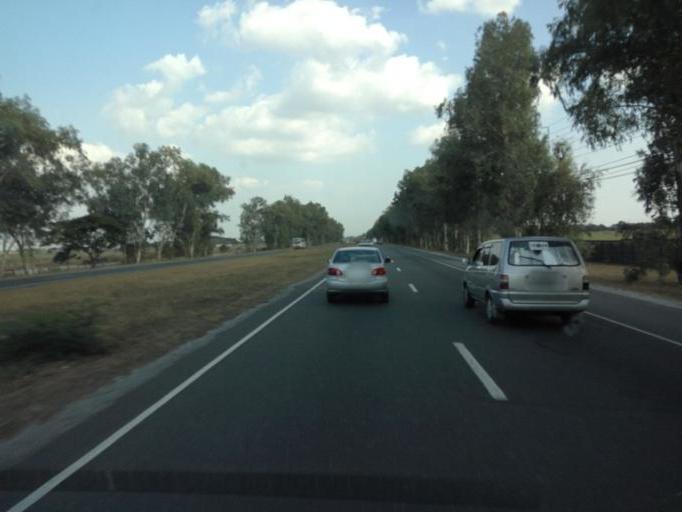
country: PH
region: Central Luzon
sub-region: Province of Pampanga
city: Culubasa
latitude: 15.1465
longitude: 120.6264
